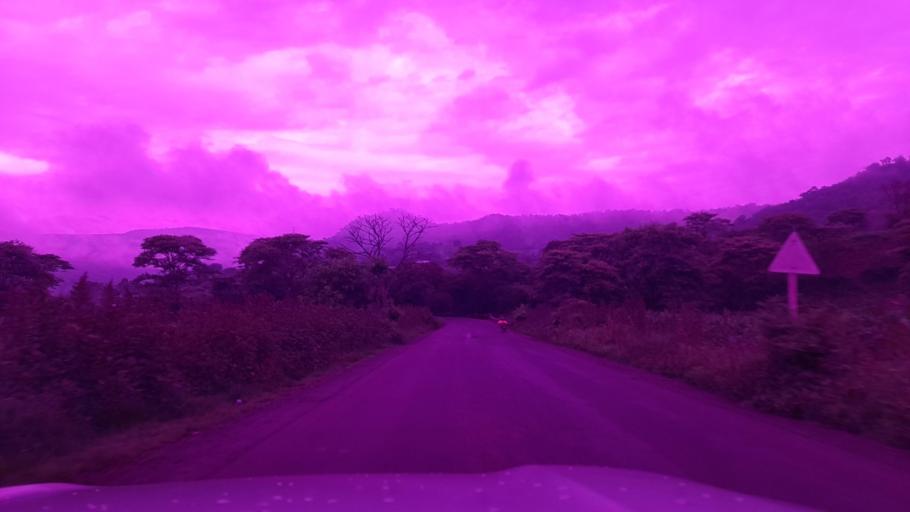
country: ET
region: Oromiya
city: Waliso
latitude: 8.2244
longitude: 37.5733
